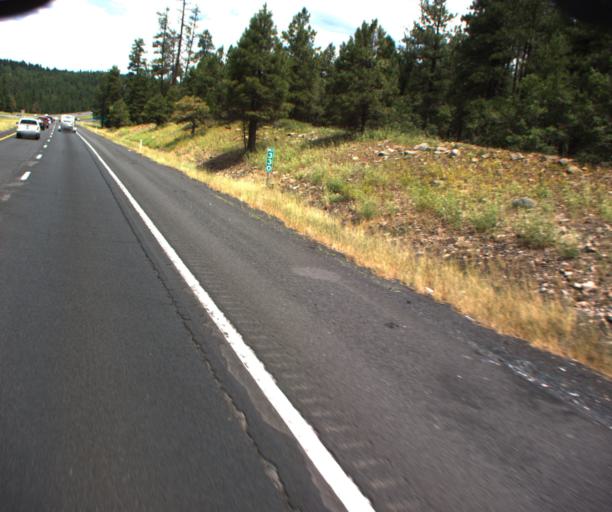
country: US
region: Arizona
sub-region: Coconino County
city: Mountainaire
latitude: 35.0360
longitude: -111.6841
